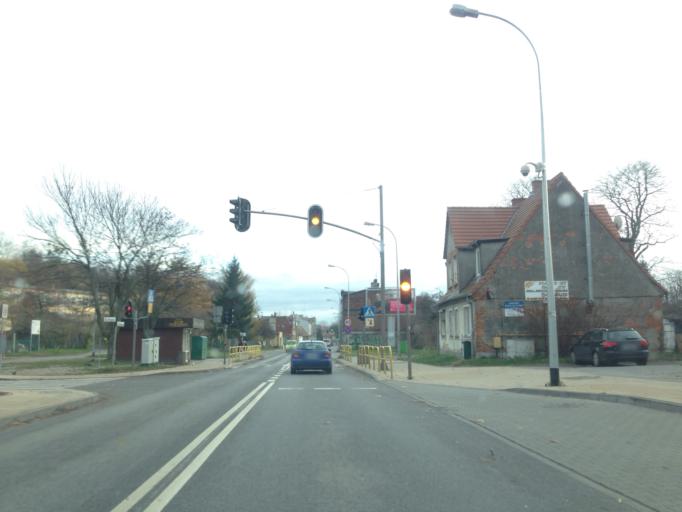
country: PL
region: Pomeranian Voivodeship
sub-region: Gdansk
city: Gdansk
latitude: 54.3302
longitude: 18.6266
